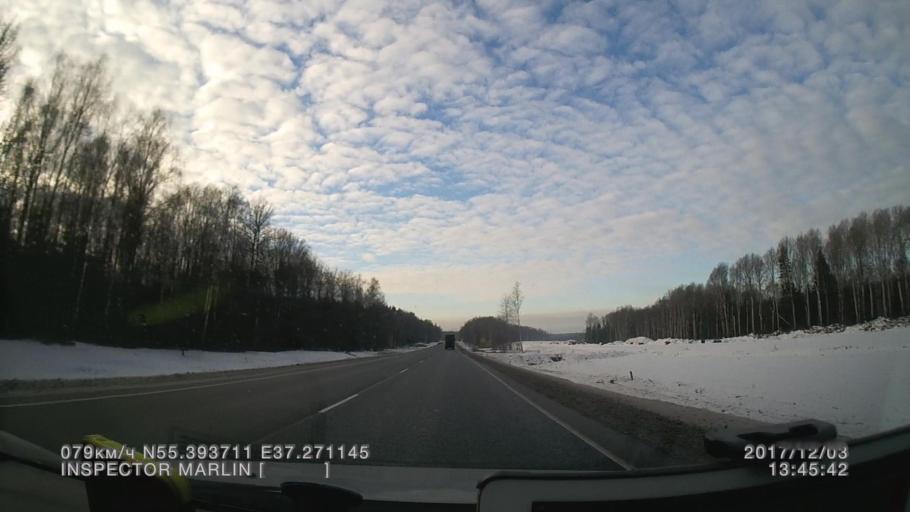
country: RU
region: Moskovskaya
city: Troitsk
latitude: 55.3937
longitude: 37.2716
